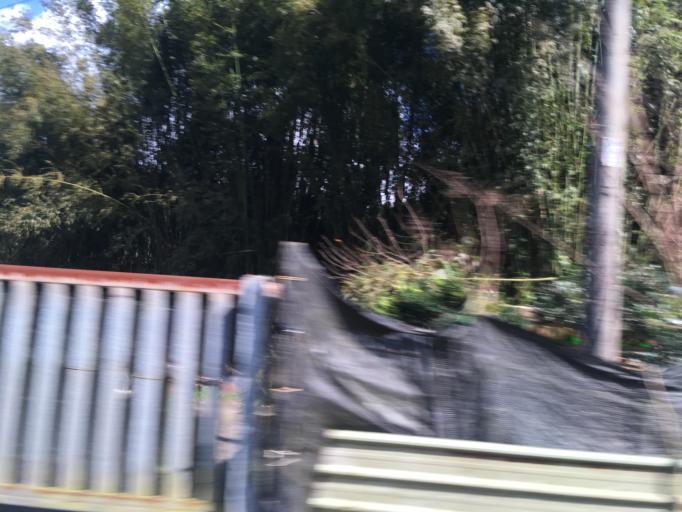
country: TW
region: Taiwan
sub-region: Yilan
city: Yilan
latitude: 24.7511
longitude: 121.6257
